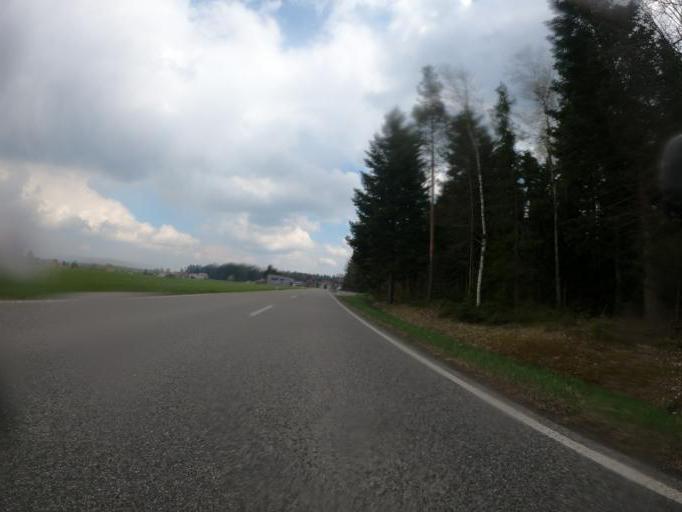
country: DE
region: Baden-Wuerttemberg
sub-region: Karlsruhe Region
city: Oberreichenbach
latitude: 48.7446
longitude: 8.6566
